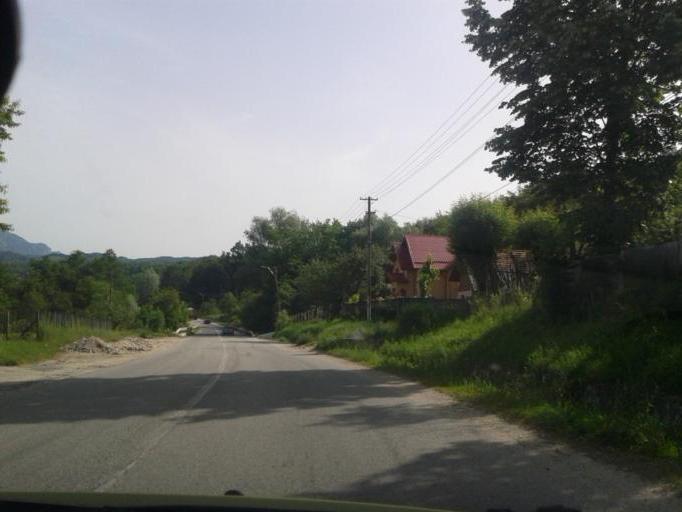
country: RO
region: Valcea
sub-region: Comuna Costesti
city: Costesti
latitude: 45.1354
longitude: 24.0646
